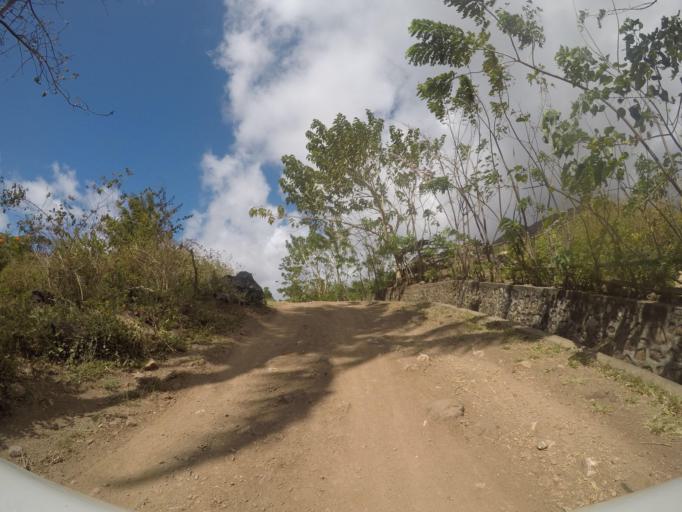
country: TL
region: Lautem
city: Lospalos
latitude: -8.5404
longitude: 126.8088
